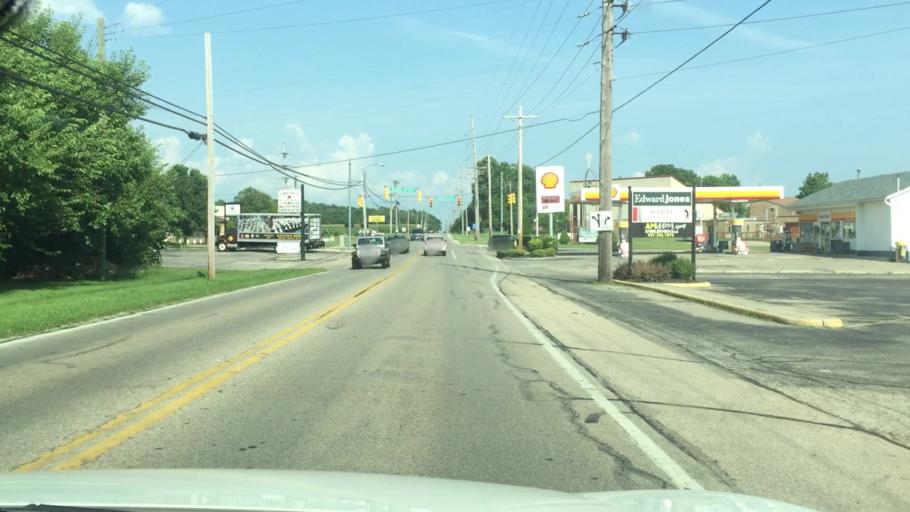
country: US
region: Ohio
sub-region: Clark County
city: Northridge
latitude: 39.9954
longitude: -83.7721
